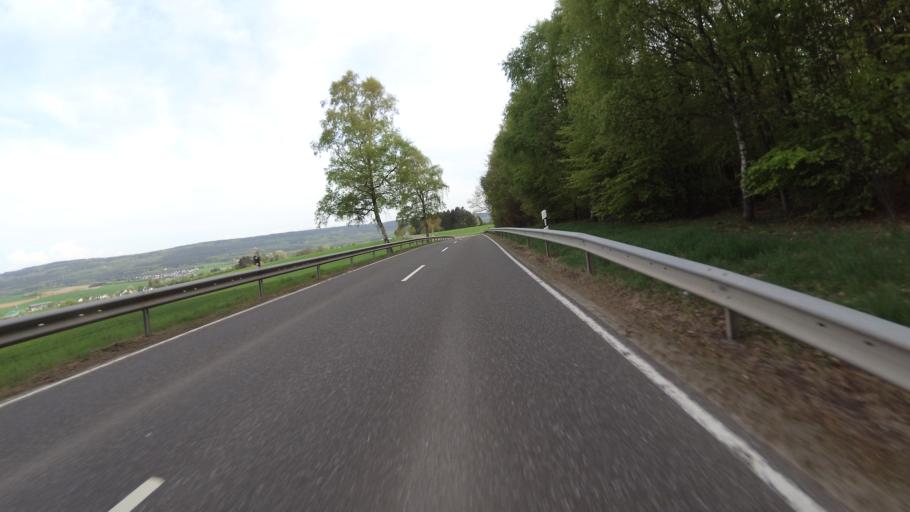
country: DE
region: Rheinland-Pfalz
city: Morbach
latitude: 49.8355
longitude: 7.1220
